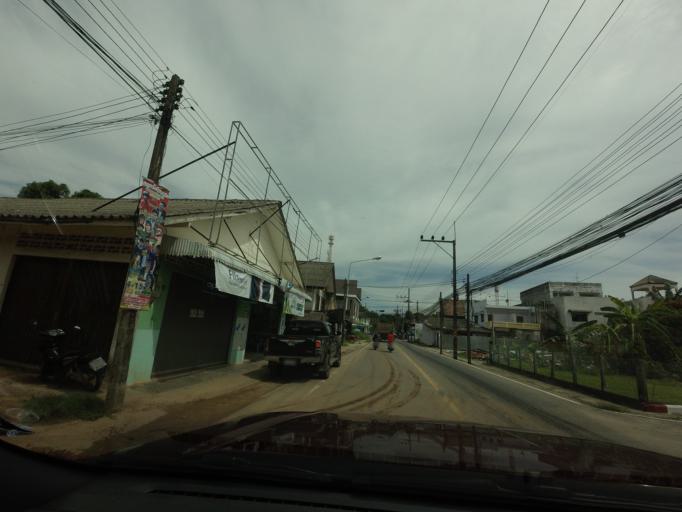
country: TH
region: Narathiwat
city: Tak Bai
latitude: 6.2589
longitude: 102.0536
